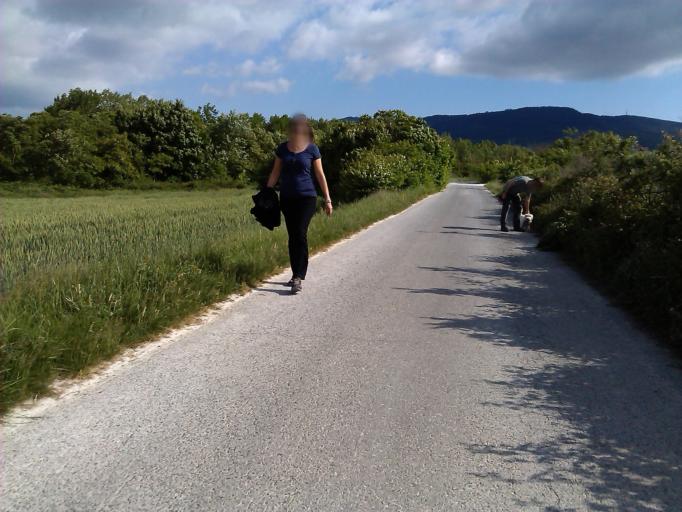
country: ES
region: Navarre
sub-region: Provincia de Navarra
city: Galar
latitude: 42.7734
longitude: -1.6942
